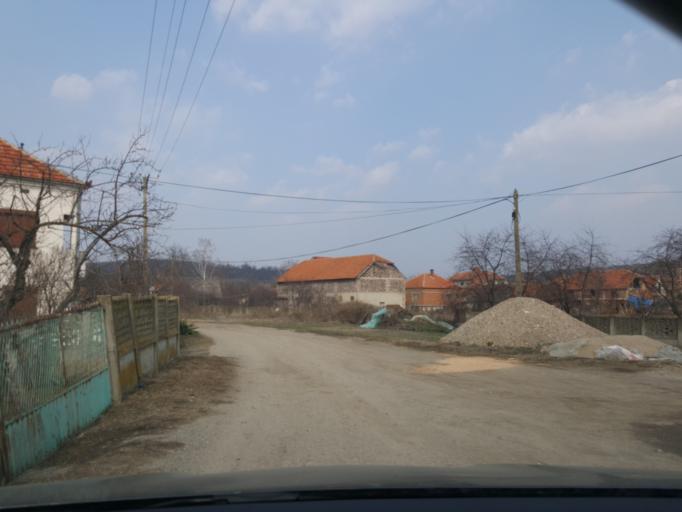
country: RS
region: Central Serbia
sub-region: Nisavski Okrug
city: Aleksinac
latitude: 43.4474
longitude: 21.7911
